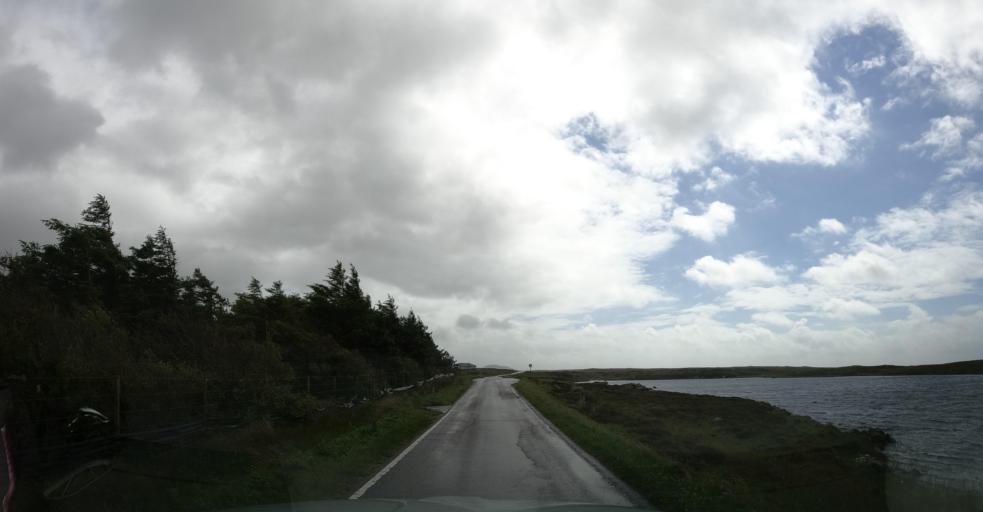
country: GB
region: Scotland
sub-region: Eilean Siar
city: Isle of South Uist
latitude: 57.2860
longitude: -7.3662
